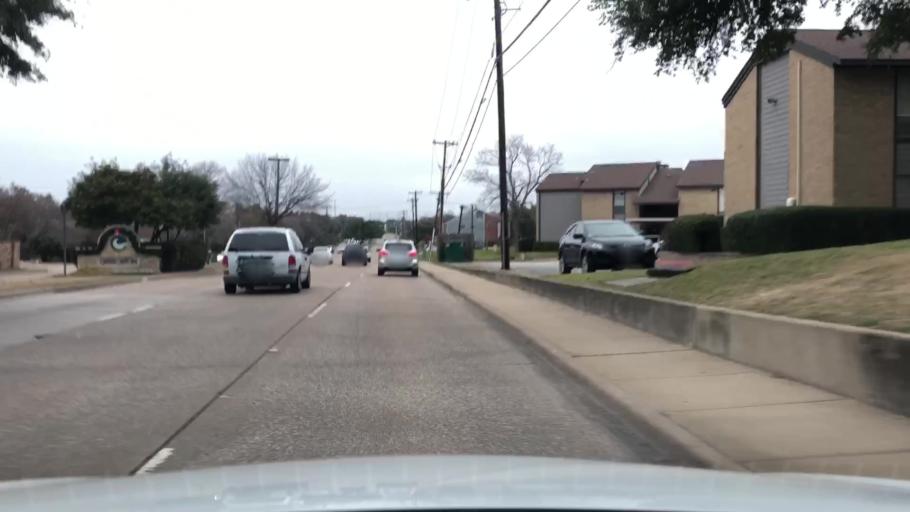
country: US
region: Texas
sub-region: Dallas County
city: Addison
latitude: 32.9618
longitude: -96.8536
